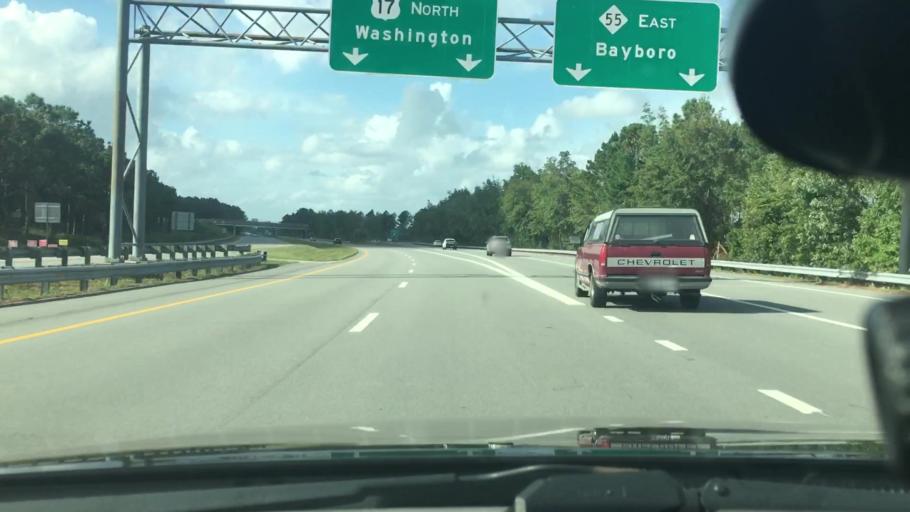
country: US
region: North Carolina
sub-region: Craven County
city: James City
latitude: 35.1114
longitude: -77.0093
